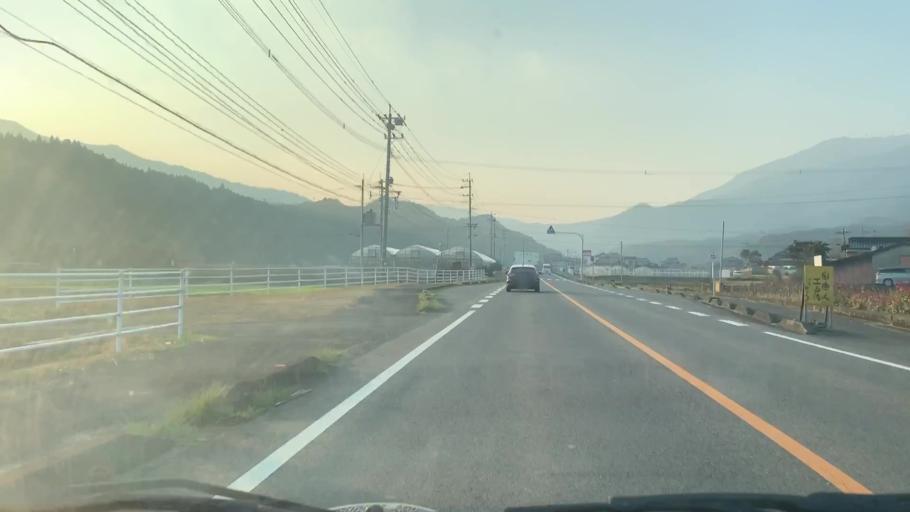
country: JP
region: Saga Prefecture
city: Takeocho-takeo
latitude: 33.2595
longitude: 130.0653
